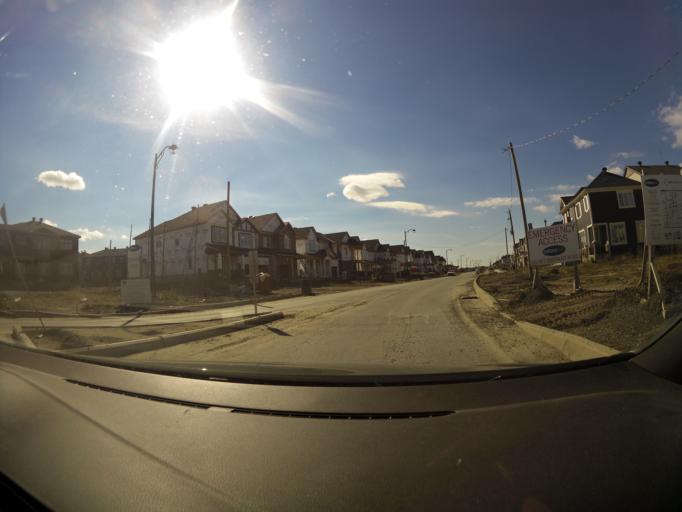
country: CA
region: Ontario
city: Bells Corners
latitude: 45.2828
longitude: -75.8894
